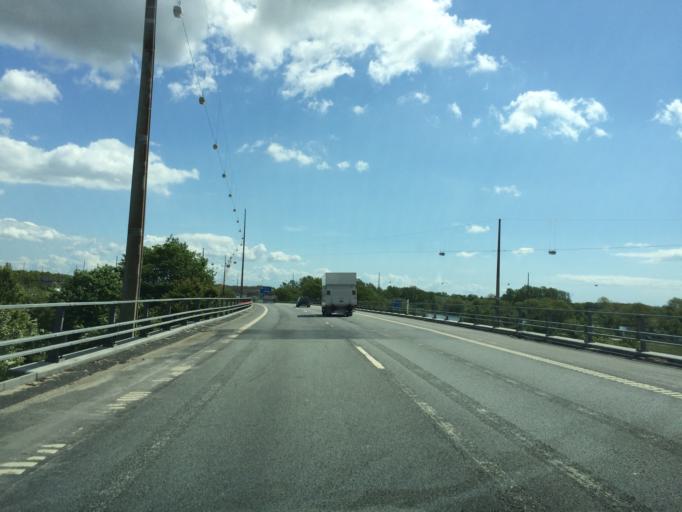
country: DK
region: Capital Region
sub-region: Vallensbaek Kommune
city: Vallensbaek
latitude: 55.6405
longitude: 12.3440
